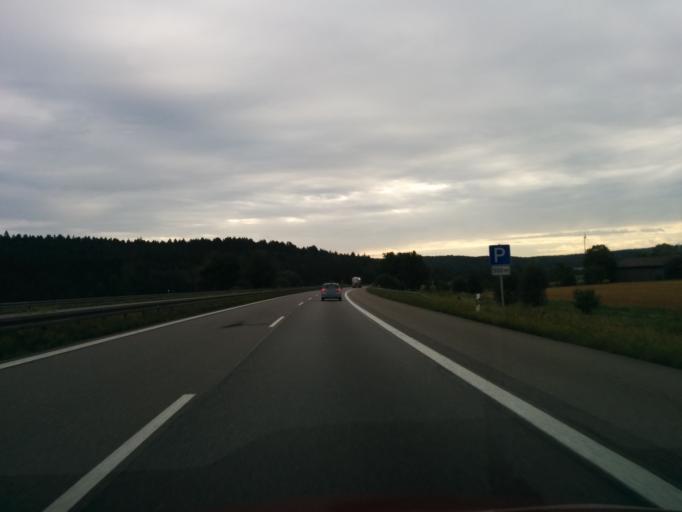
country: DE
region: Bavaria
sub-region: Upper Palatinate
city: Hohenfels
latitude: 49.1693
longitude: 11.8207
